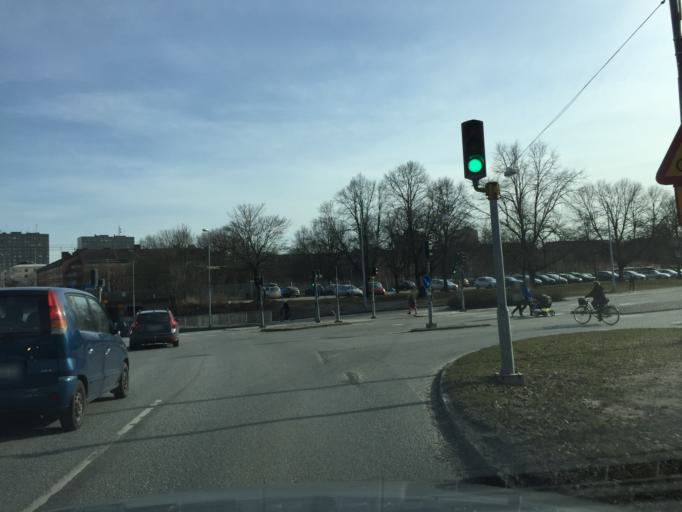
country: SE
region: OErebro
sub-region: Orebro Kommun
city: Orebro
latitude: 59.2715
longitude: 15.2021
